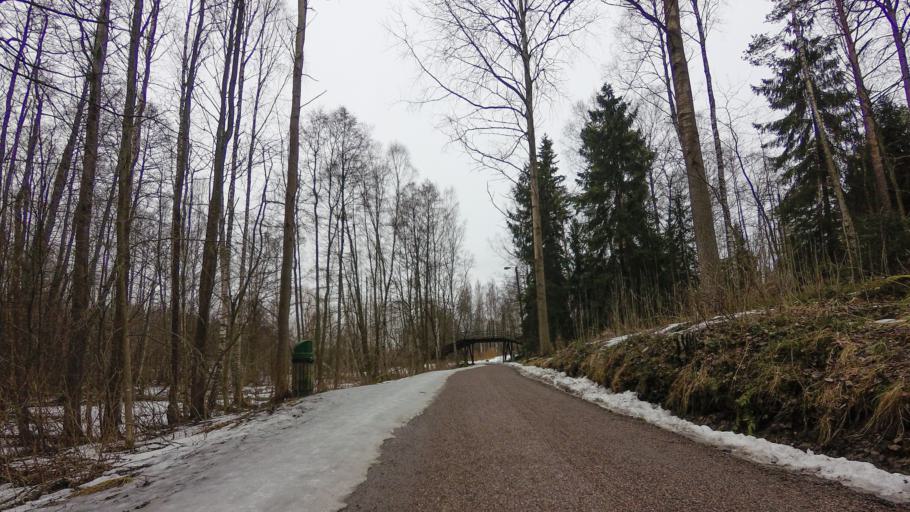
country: FI
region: Uusimaa
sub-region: Helsinki
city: Vantaa
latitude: 60.2086
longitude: 25.0284
